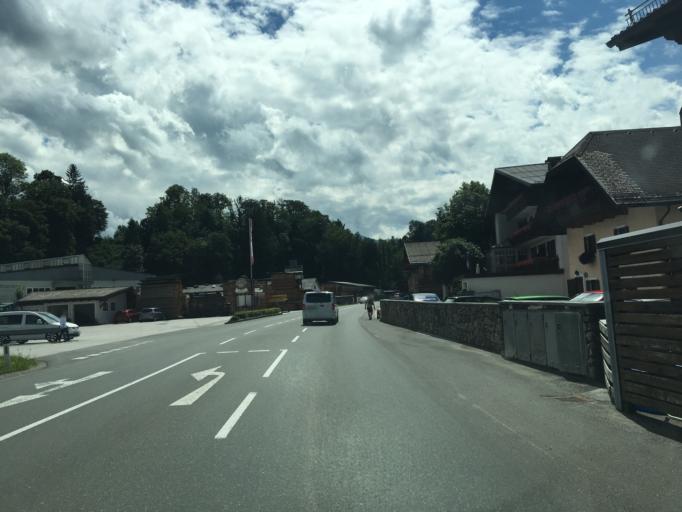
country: AT
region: Salzburg
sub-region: Politischer Bezirk Hallein
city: Adnet
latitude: 47.7094
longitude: 13.1327
